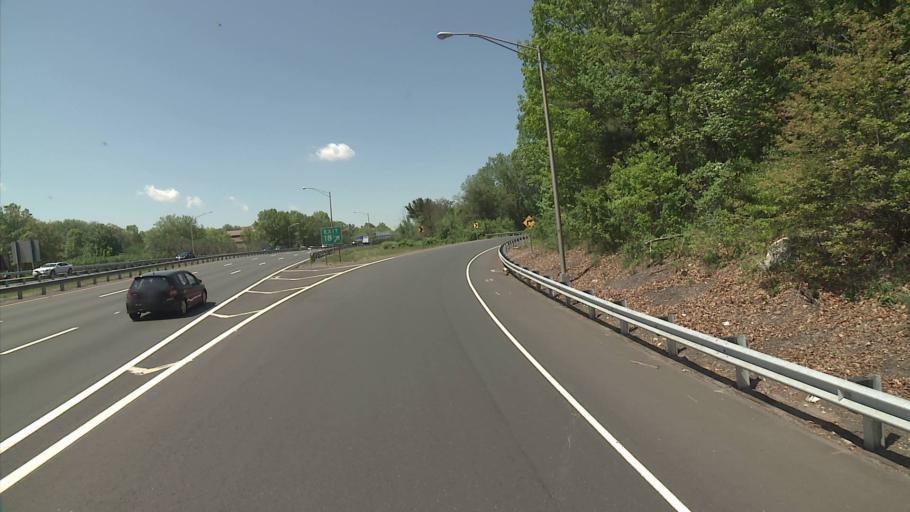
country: US
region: Connecticut
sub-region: New Haven County
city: Waterbury
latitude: 41.5493
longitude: -73.0618
